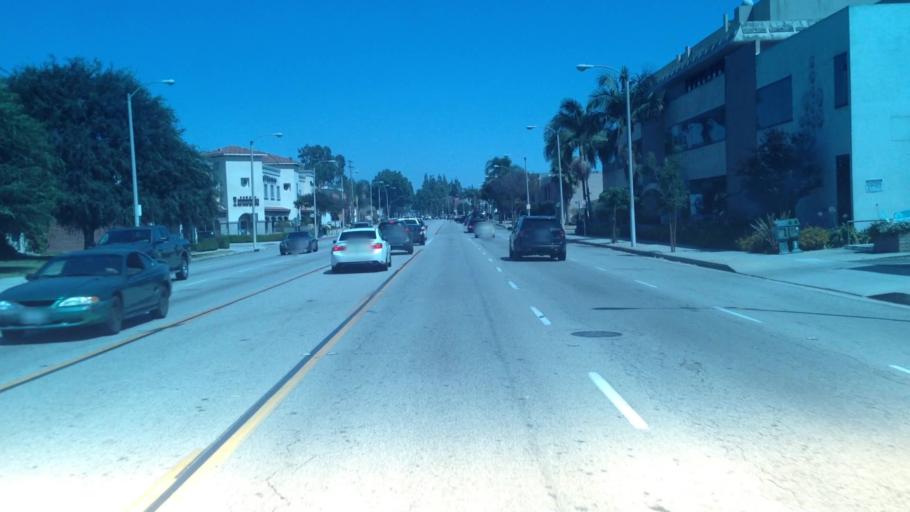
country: US
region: California
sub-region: Los Angeles County
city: Downey
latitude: 33.9529
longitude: -118.1289
